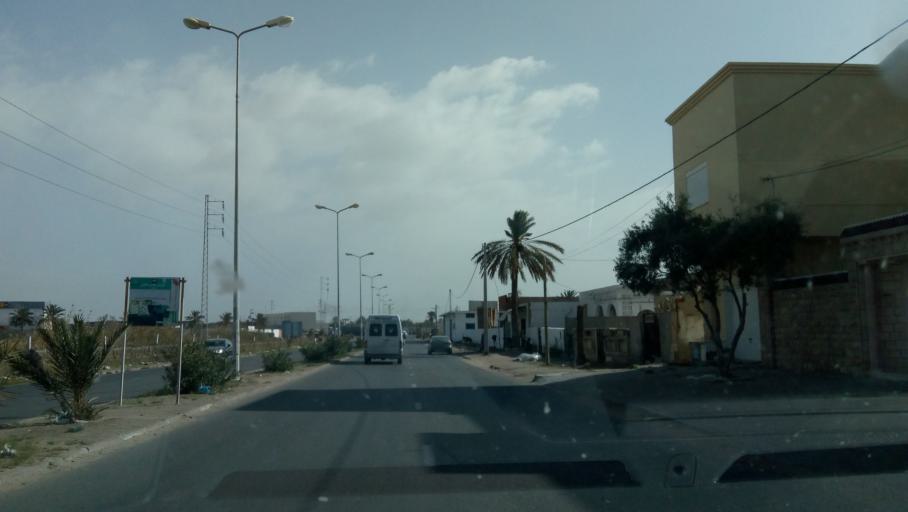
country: TN
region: Qabis
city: Gabes
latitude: 33.8921
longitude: 10.0745
